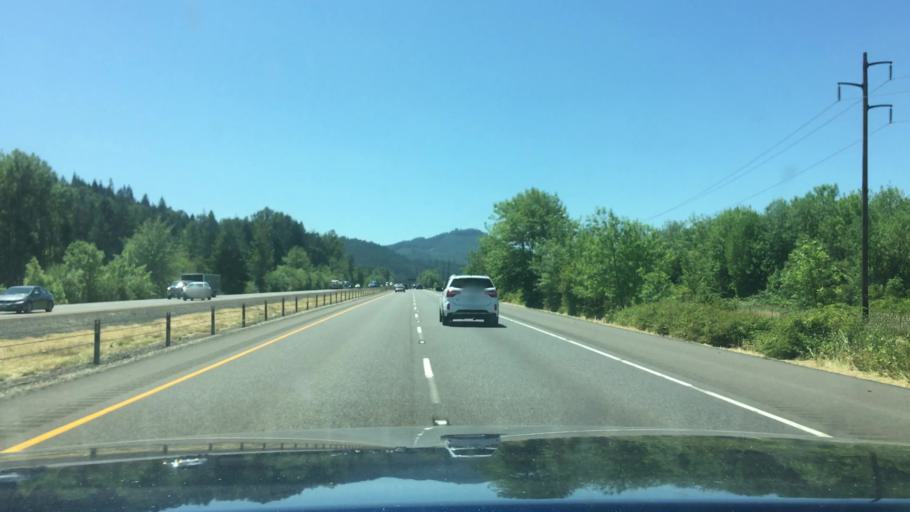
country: US
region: Oregon
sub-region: Lane County
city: Cottage Grove
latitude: 43.7607
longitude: -123.0854
